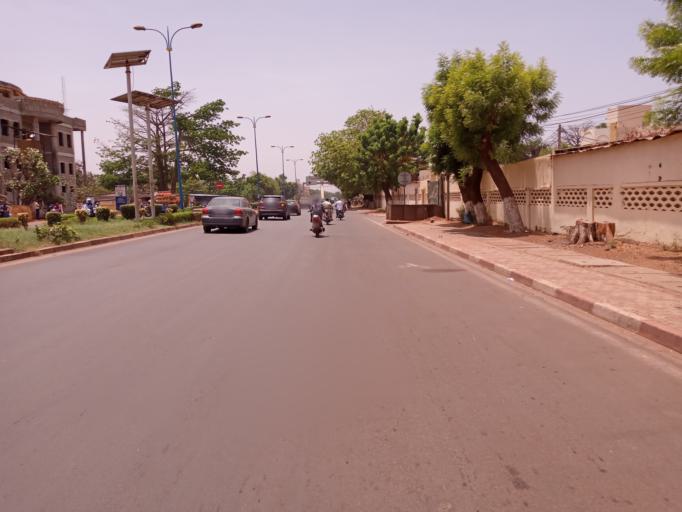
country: ML
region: Bamako
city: Bamako
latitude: 12.6348
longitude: -8.0072
